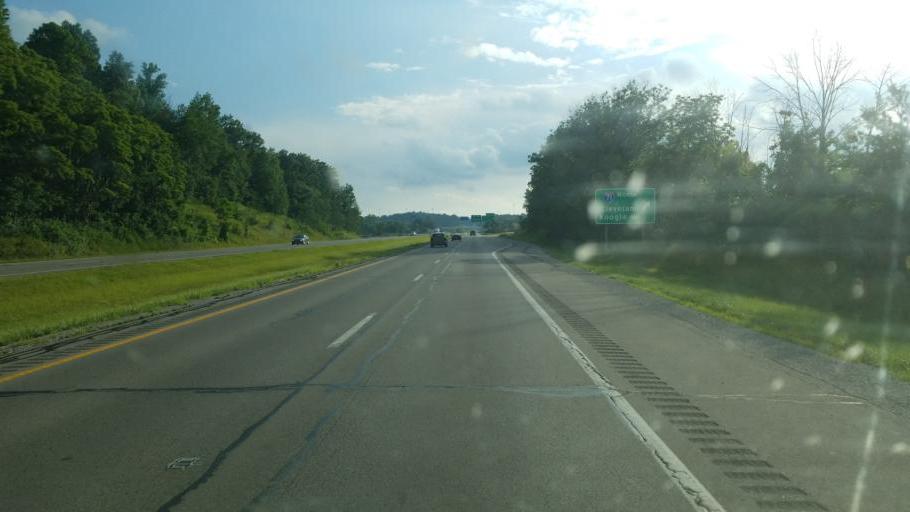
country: US
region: Ohio
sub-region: Richland County
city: Lincoln Heights
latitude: 40.7862
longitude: -82.4002
